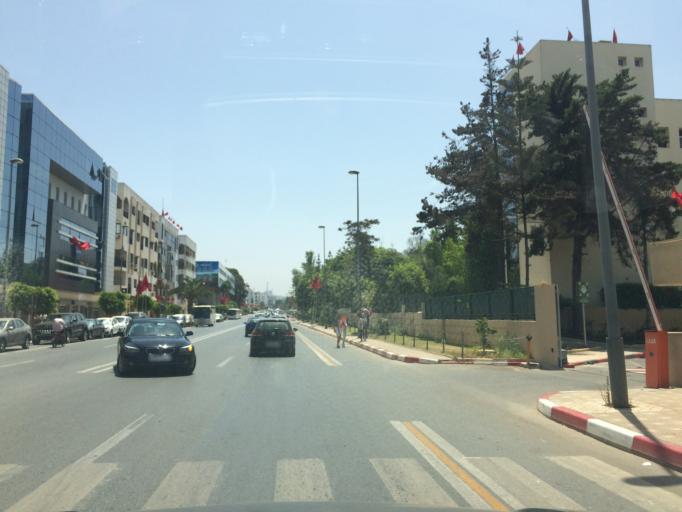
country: MA
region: Rabat-Sale-Zemmour-Zaer
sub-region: Rabat
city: Rabat
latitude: 33.9948
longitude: -6.8514
